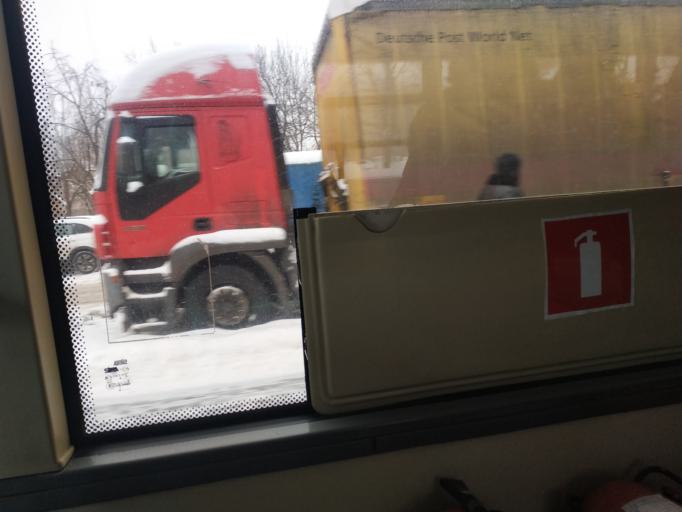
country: RU
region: Moscow
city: Kolomenskoye
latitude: 55.6744
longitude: 37.6792
